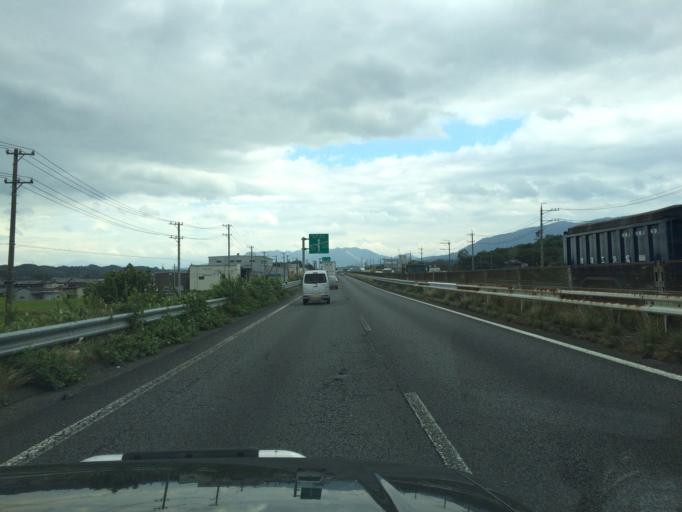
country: JP
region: Mie
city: Ueno-ebisumachi
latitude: 34.8012
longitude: 136.1844
